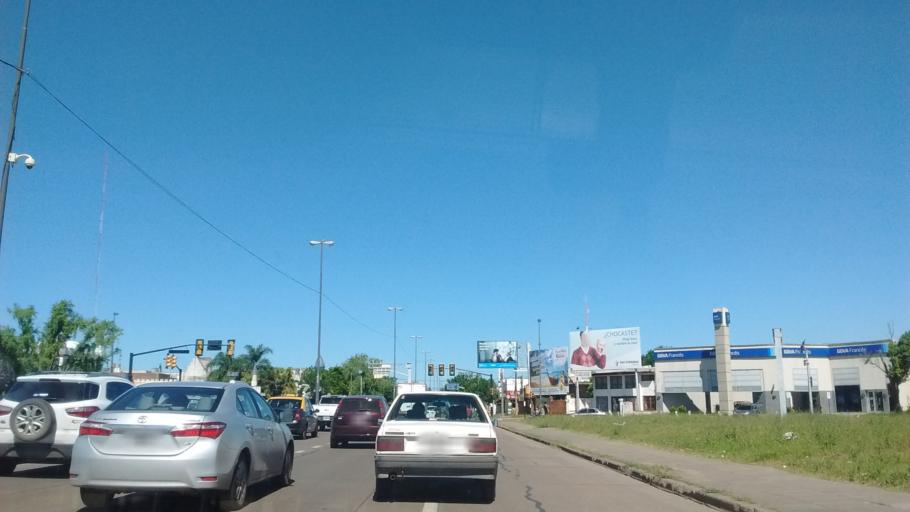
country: AR
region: Santa Fe
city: Granadero Baigorria
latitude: -32.9313
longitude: -60.7227
